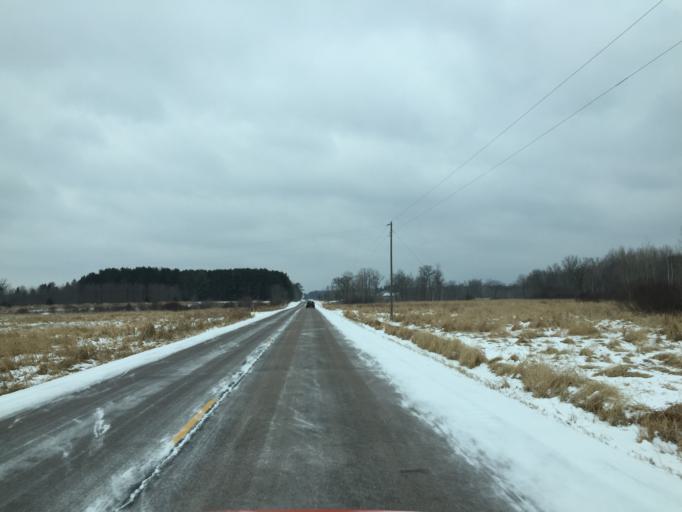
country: US
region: Minnesota
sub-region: Mille Lacs County
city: Vineland
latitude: 46.0774
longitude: -93.7374
